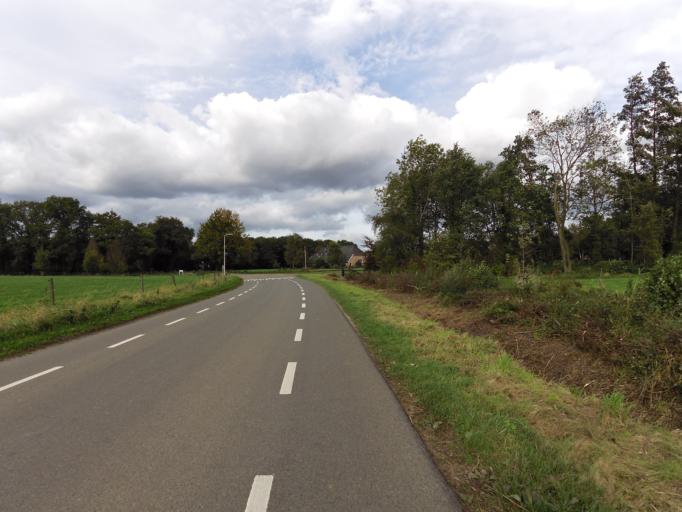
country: NL
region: Gelderland
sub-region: Gemeente Bronckhorst
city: Baak
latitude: 52.0980
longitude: 6.2494
